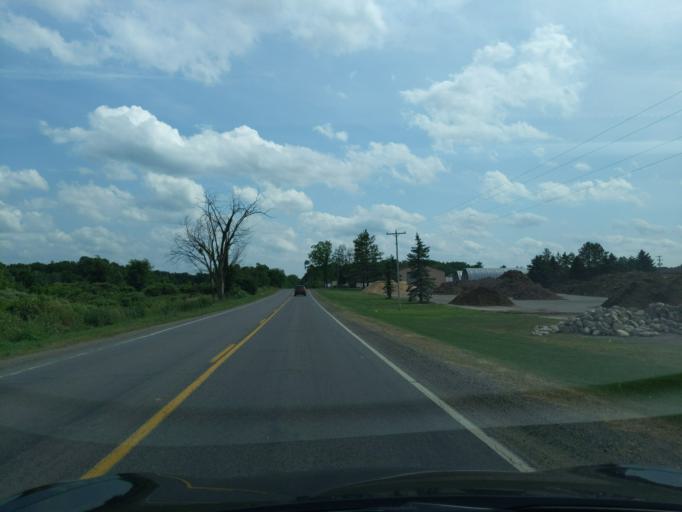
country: US
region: Michigan
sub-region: Eaton County
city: Dimondale
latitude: 42.6528
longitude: -84.6030
